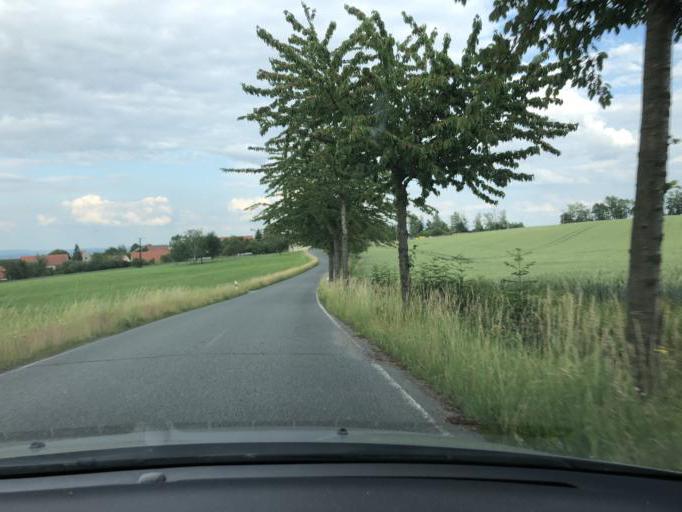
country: DE
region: Saxony
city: Wilsdruff
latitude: 51.0542
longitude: 13.5875
